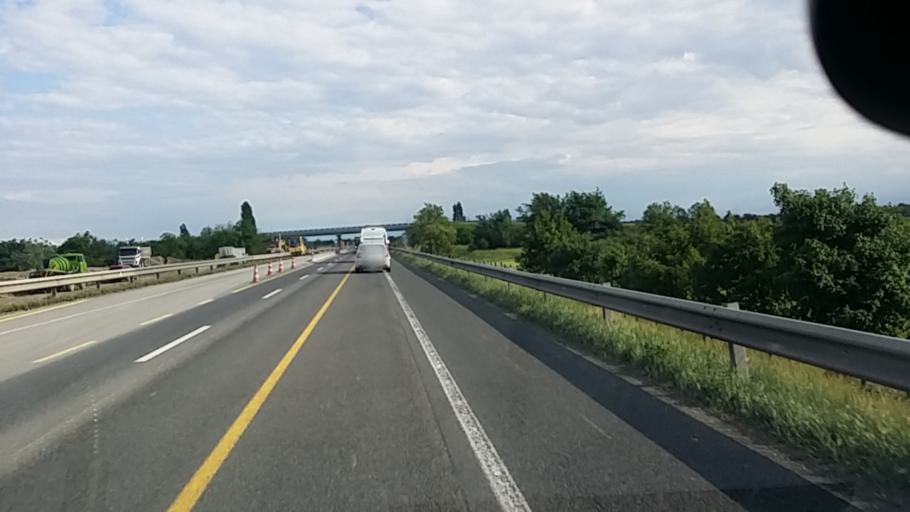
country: HU
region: Gyor-Moson-Sopron
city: Rajka
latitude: 47.9254
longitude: 17.1737
